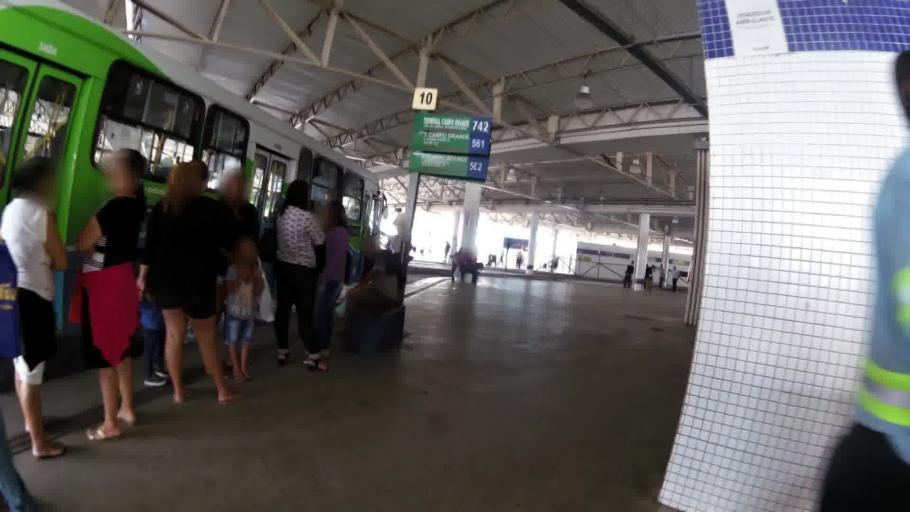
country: BR
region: Espirito Santo
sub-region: Vitoria
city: Vitoria
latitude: -20.3302
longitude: -40.3531
